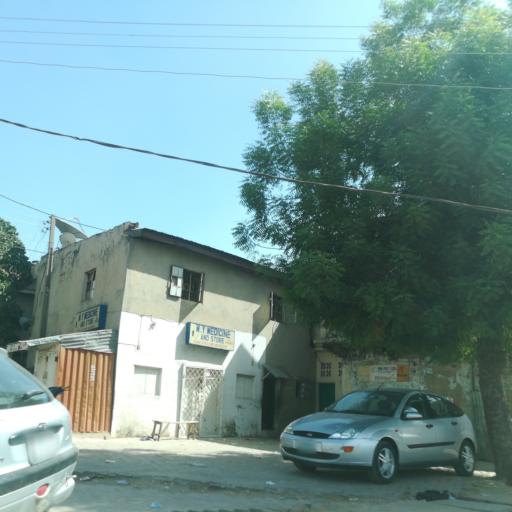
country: NG
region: Kano
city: Kano
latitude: 11.9996
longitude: 8.5245
